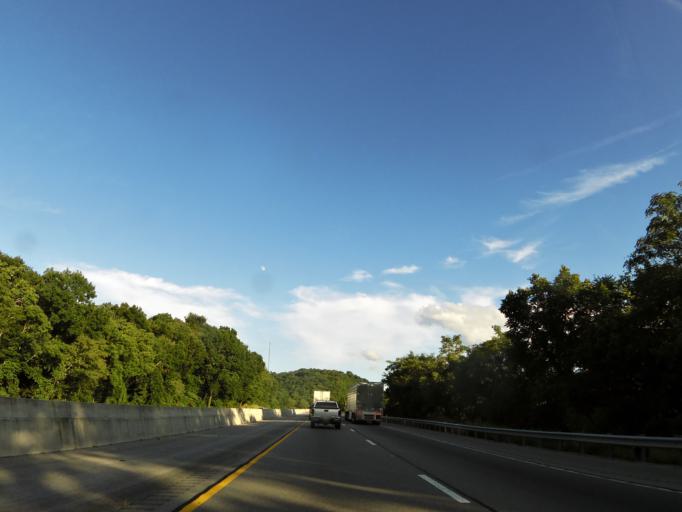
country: US
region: Tennessee
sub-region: Putnam County
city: Lafayette
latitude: 36.1340
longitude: -85.7835
